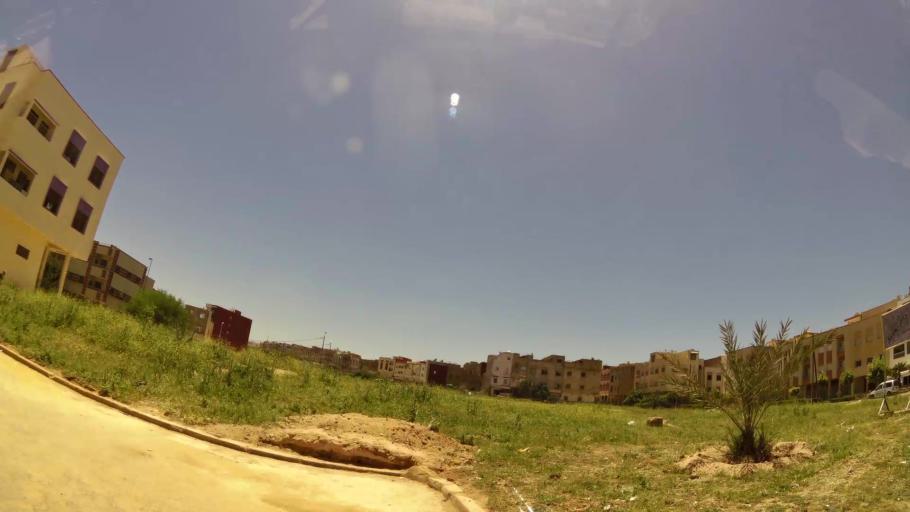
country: MA
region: Meknes-Tafilalet
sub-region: Meknes
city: Meknes
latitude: 33.8571
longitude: -5.5590
